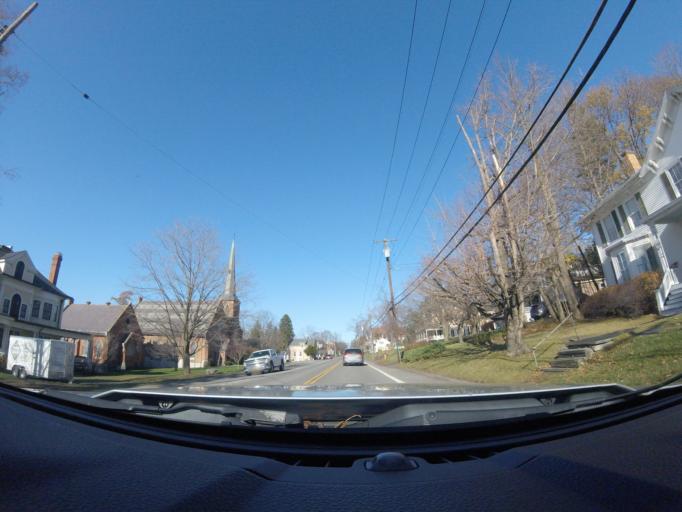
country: US
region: New York
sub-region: Cayuga County
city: Union Springs
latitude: 42.7518
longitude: -76.7017
